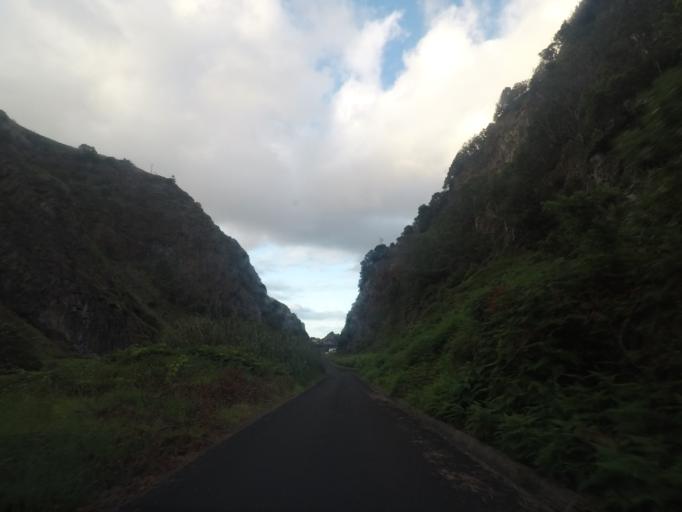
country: PT
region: Madeira
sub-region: Porto Moniz
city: Porto Moniz
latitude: 32.8513
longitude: -17.1592
